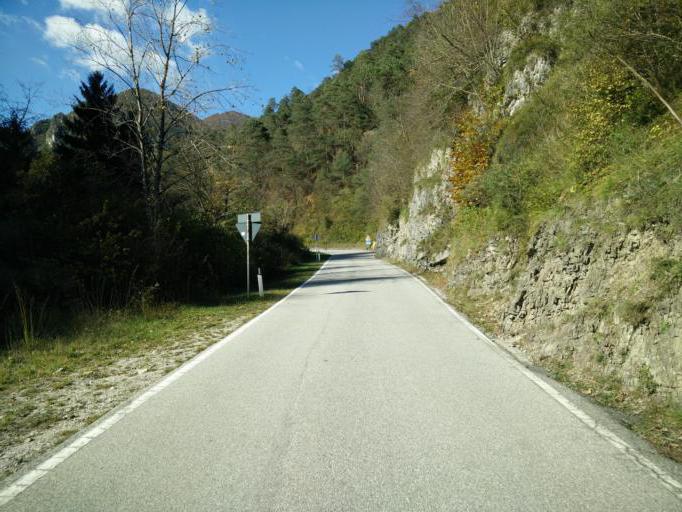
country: IT
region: Lombardy
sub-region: Provincia di Brescia
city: Valvestino
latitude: 45.7472
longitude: 10.5895
